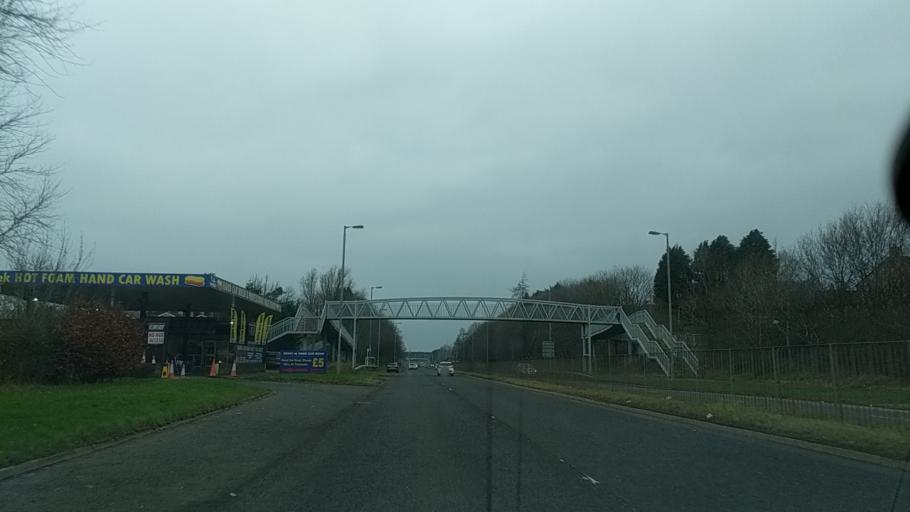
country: GB
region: Scotland
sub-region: South Lanarkshire
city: East Kilbride
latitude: 55.7628
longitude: -4.1990
